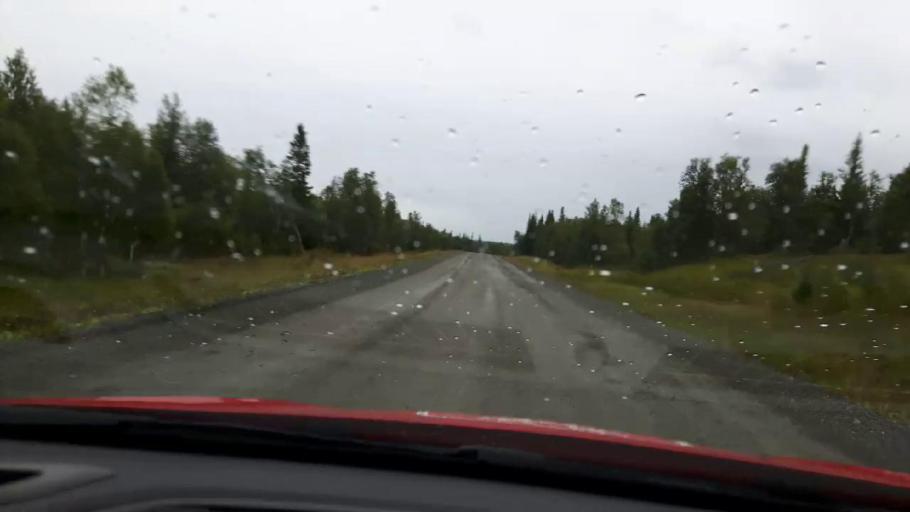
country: NO
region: Nord-Trondelag
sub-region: Meraker
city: Meraker
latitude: 63.5634
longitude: 12.2886
